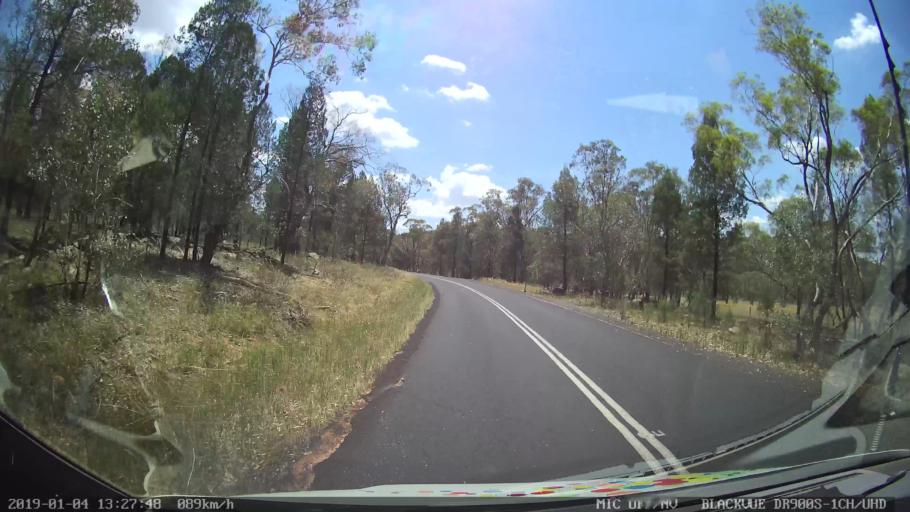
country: AU
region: New South Wales
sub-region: Parkes
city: Peak Hill
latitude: -32.6638
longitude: 148.5591
